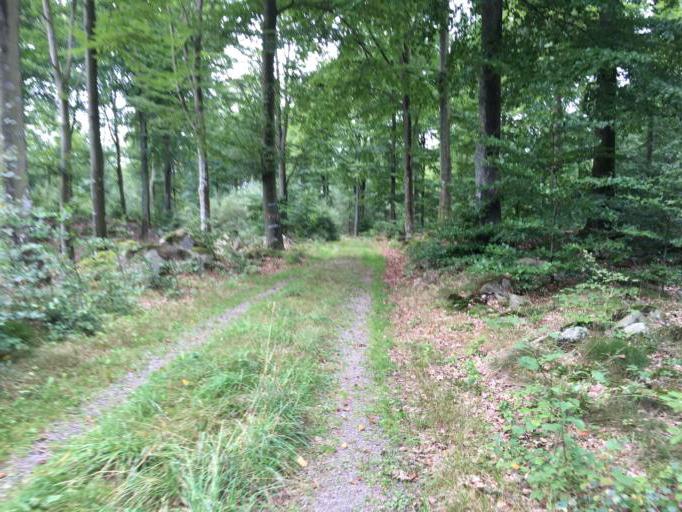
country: SE
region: Skane
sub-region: Hoors Kommun
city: Hoeoer
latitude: 55.9873
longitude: 13.4744
